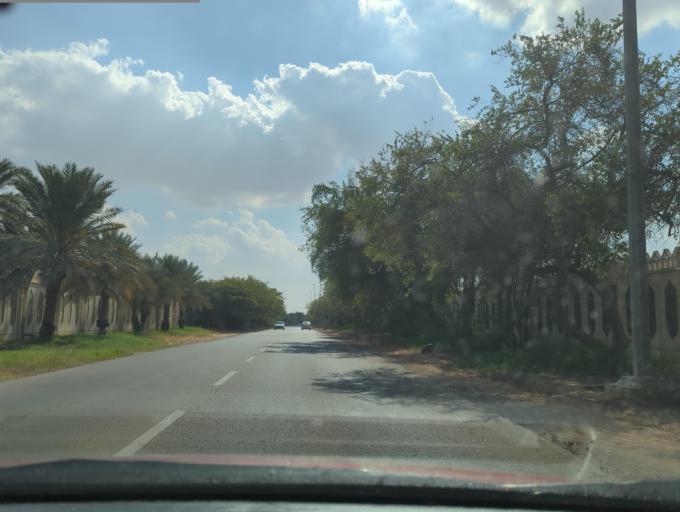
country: AE
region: Abu Dhabi
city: Al Ain
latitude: 24.1707
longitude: 55.6504
